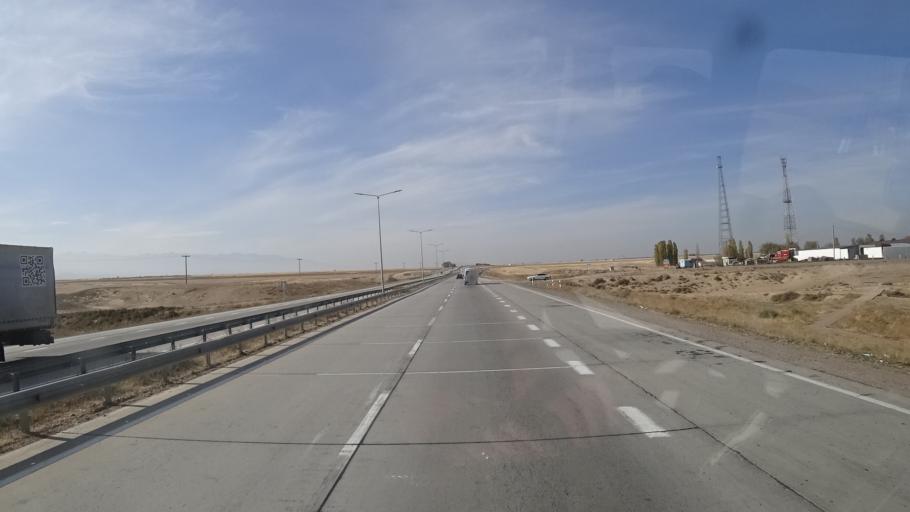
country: KZ
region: Zhambyl
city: Merke
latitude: 42.8895
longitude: 72.9840
